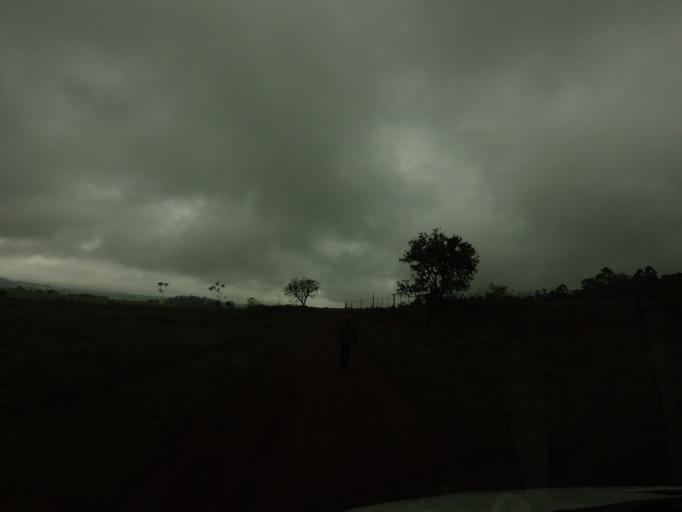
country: SZ
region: Hhohho
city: Lobamba
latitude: -26.4716
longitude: 31.1858
